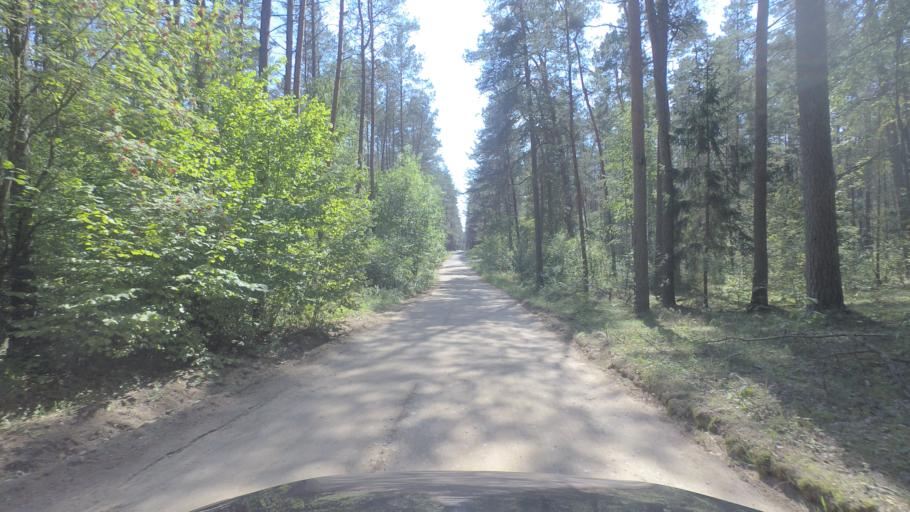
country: LT
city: Nemencine
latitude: 54.8458
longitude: 25.4980
